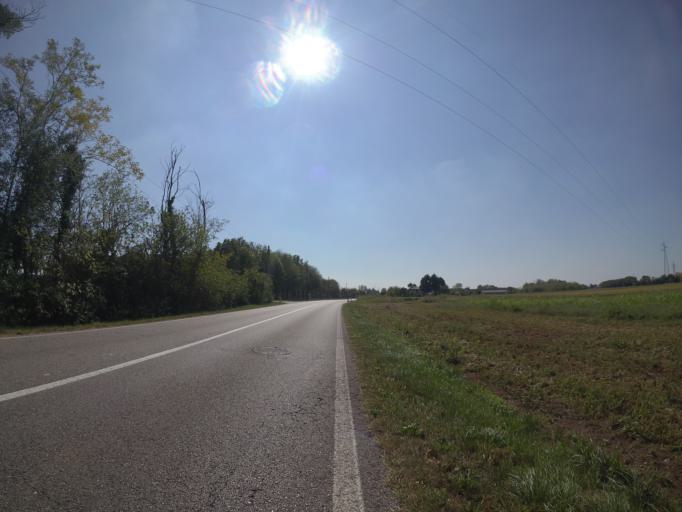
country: IT
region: Friuli Venezia Giulia
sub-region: Provincia di Udine
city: Codroipo
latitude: 45.9803
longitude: 12.9927
